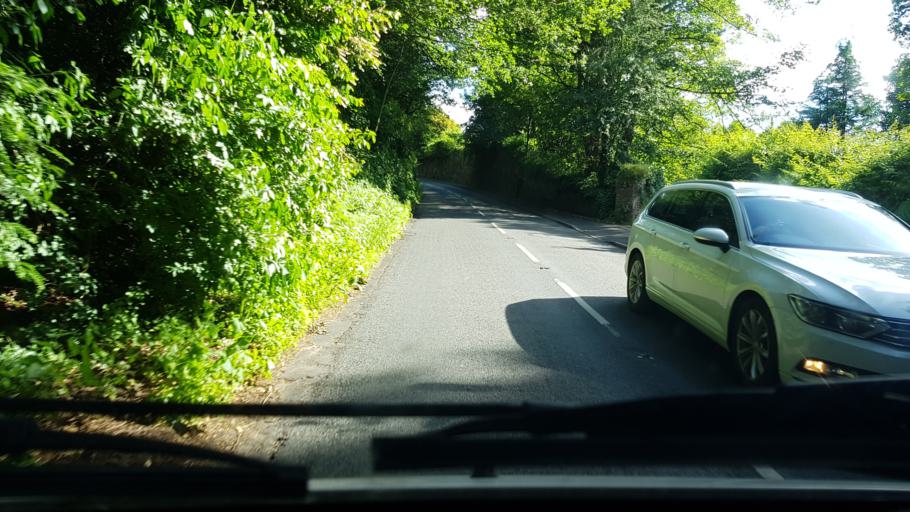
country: GB
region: England
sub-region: Worcestershire
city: Bewdley
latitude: 52.3705
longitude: -2.3125
